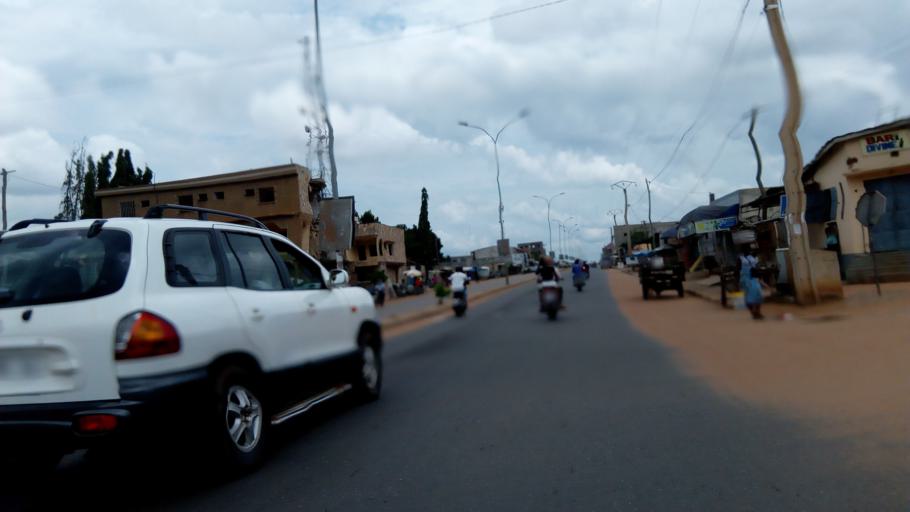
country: TG
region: Maritime
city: Lome
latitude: 6.2117
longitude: 1.1769
